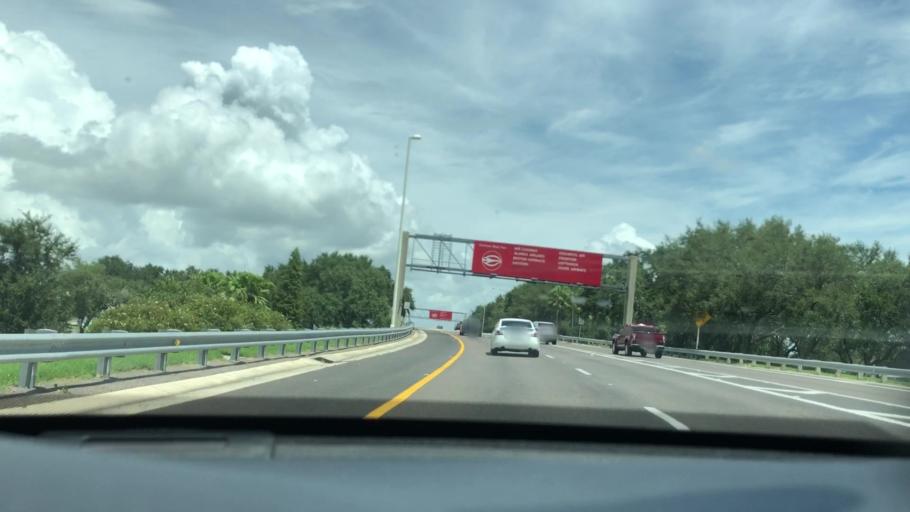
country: US
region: Florida
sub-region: Hillsborough County
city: Town 'n' Country
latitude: 27.9653
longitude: -82.5390
